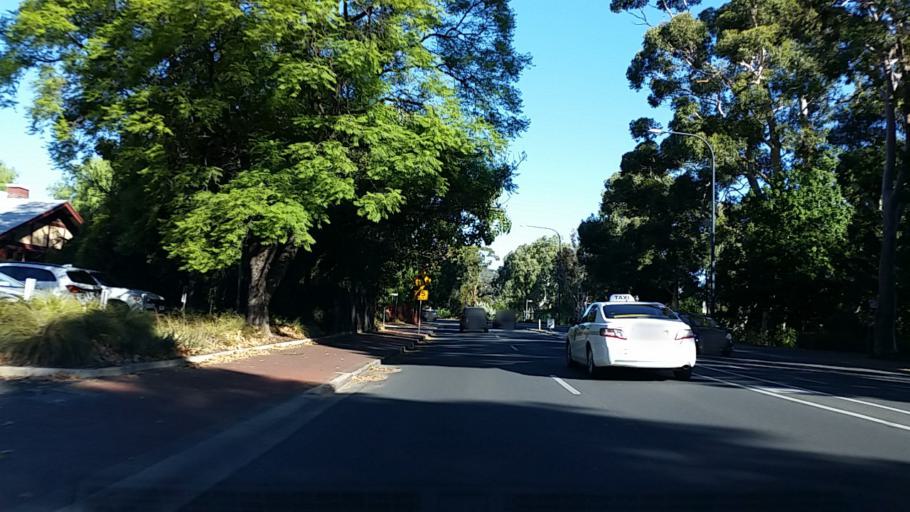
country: AU
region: South Australia
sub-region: Mitcham
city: Hawthorn
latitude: -34.9770
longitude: 138.6096
